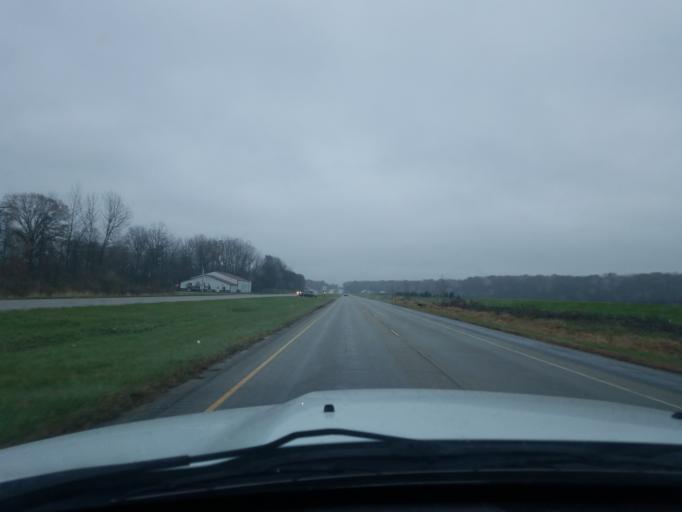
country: US
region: Indiana
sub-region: Cass County
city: Logansport
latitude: 40.7333
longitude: -86.3344
